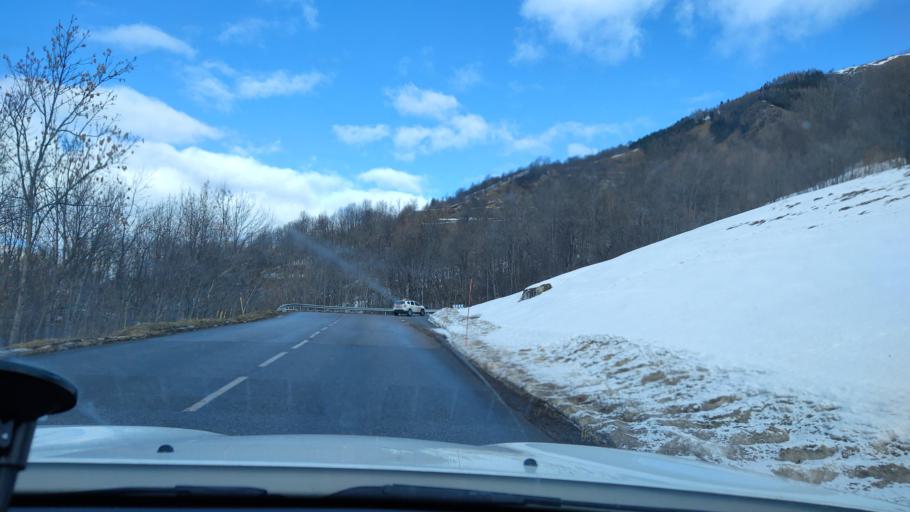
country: FR
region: Rhone-Alpes
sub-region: Departement de la Savoie
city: Saint-Martin-de-Belleville
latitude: 45.3855
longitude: 6.5032
